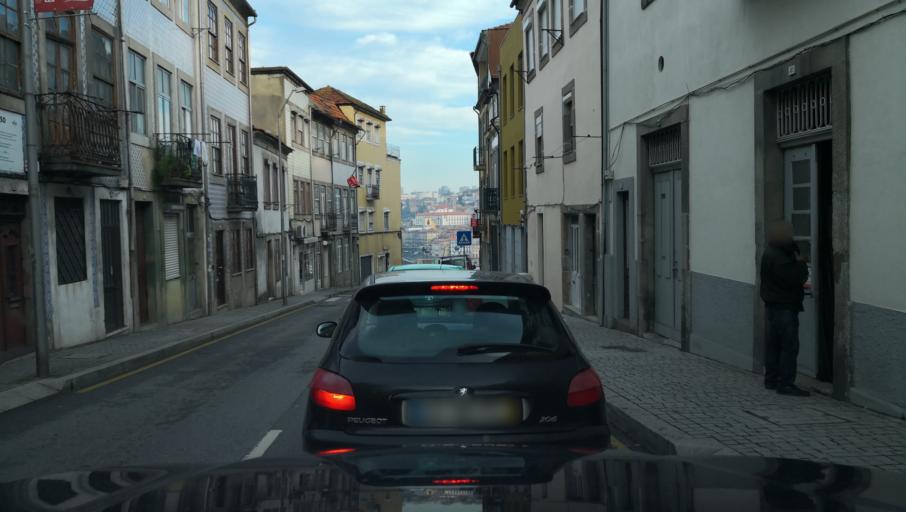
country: PT
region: Porto
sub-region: Vila Nova de Gaia
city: Vila Nova de Gaia
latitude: 41.1349
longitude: -8.6111
